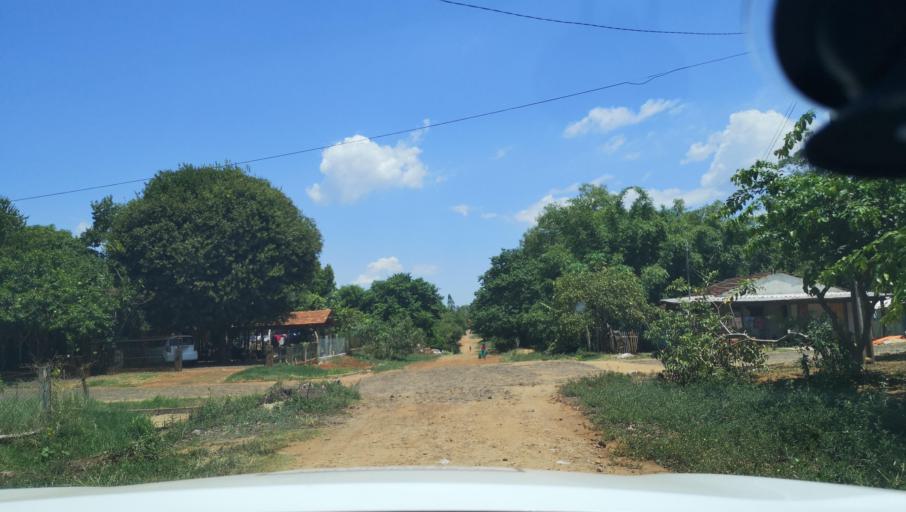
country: PY
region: Itapua
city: Carmen del Parana
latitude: -27.1660
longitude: -56.2452
